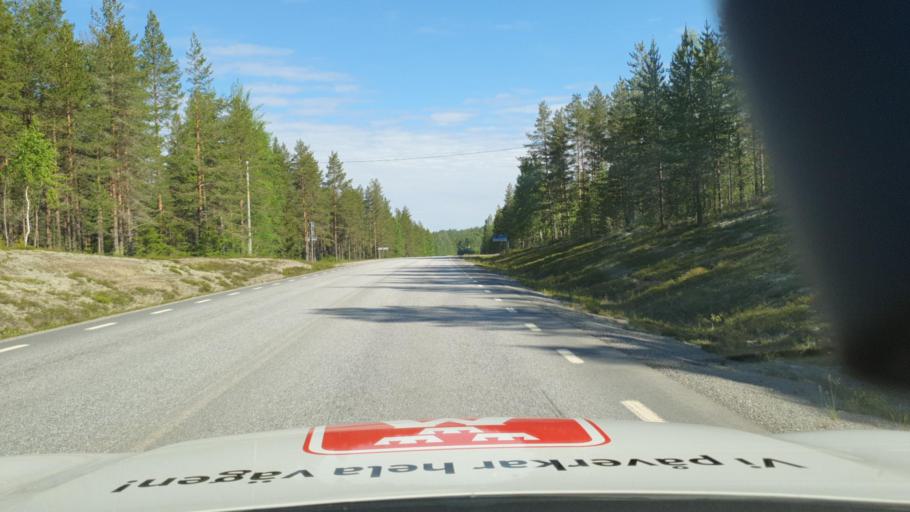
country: SE
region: Vaesterbotten
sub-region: Vannas Kommun
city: Vannasby
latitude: 64.0639
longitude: 19.9924
